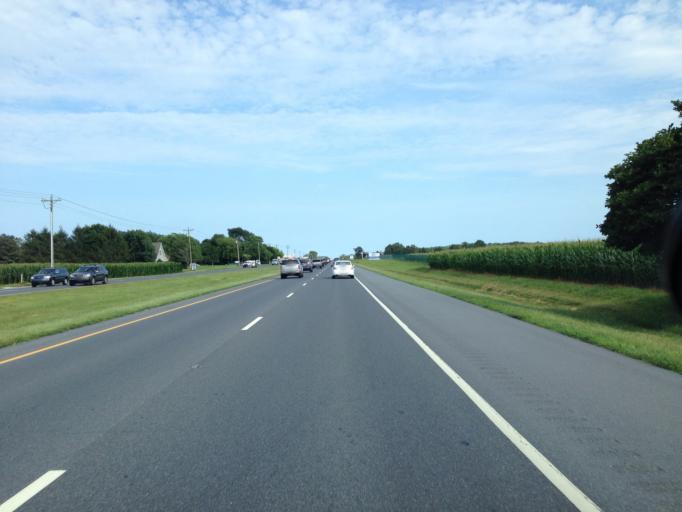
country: US
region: Delaware
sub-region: Sussex County
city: Milton
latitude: 38.7799
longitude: -75.2337
